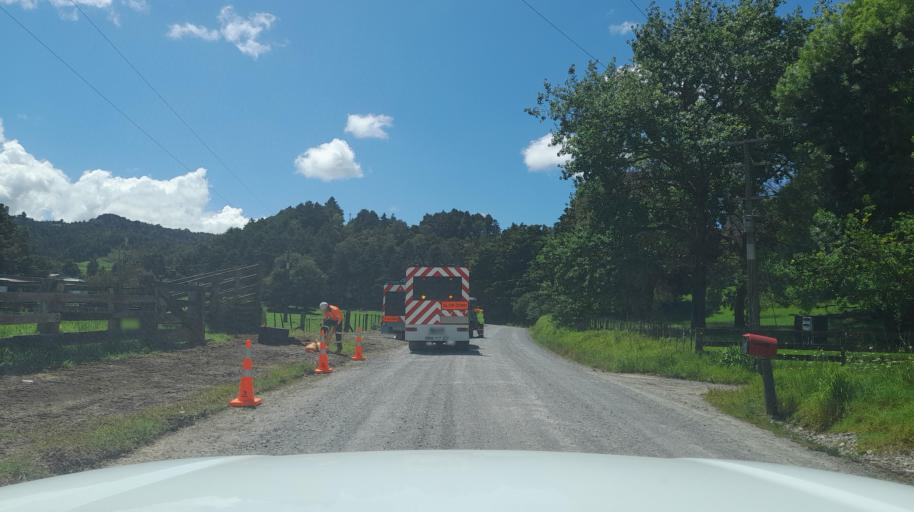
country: NZ
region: Northland
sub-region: Far North District
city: Kaitaia
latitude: -35.1106
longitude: 173.3953
